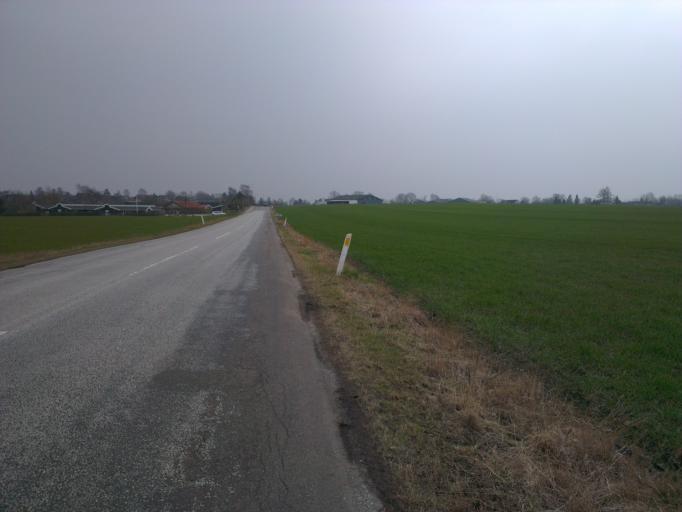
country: DK
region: Capital Region
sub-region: Egedal Kommune
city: Olstykke
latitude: 55.8028
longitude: 12.1113
